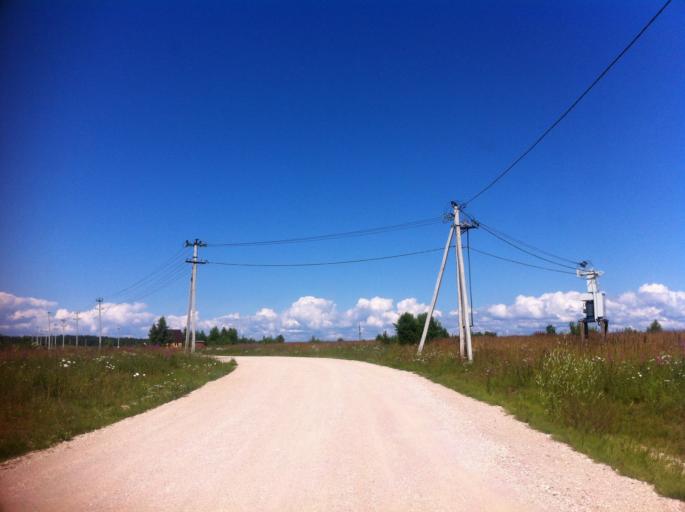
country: RU
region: Pskov
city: Izborsk
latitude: 57.8256
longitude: 27.9659
